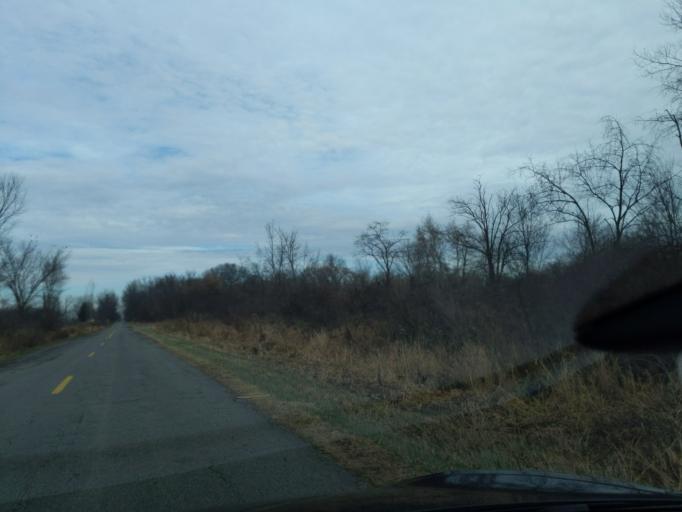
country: US
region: Michigan
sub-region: Ingham County
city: Leslie
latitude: 42.4932
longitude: -84.5023
